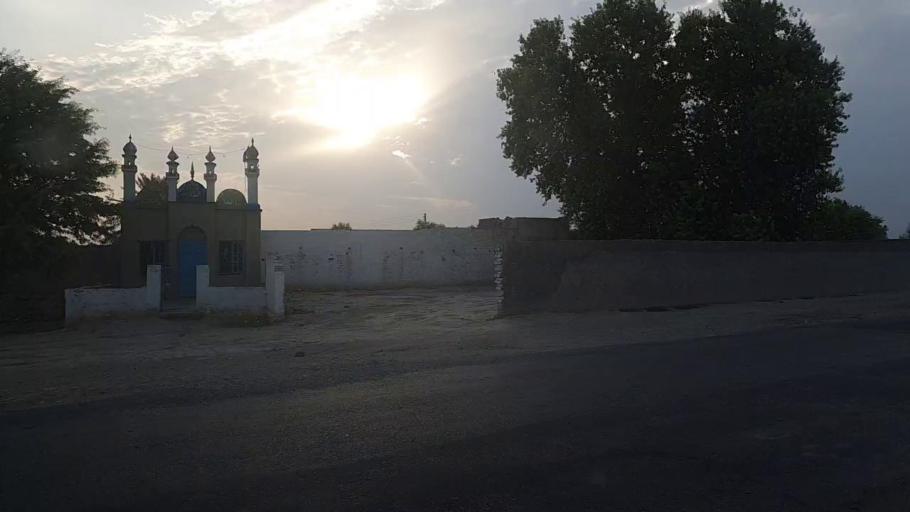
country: PK
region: Sindh
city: Ubauro
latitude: 28.3539
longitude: 69.7738
